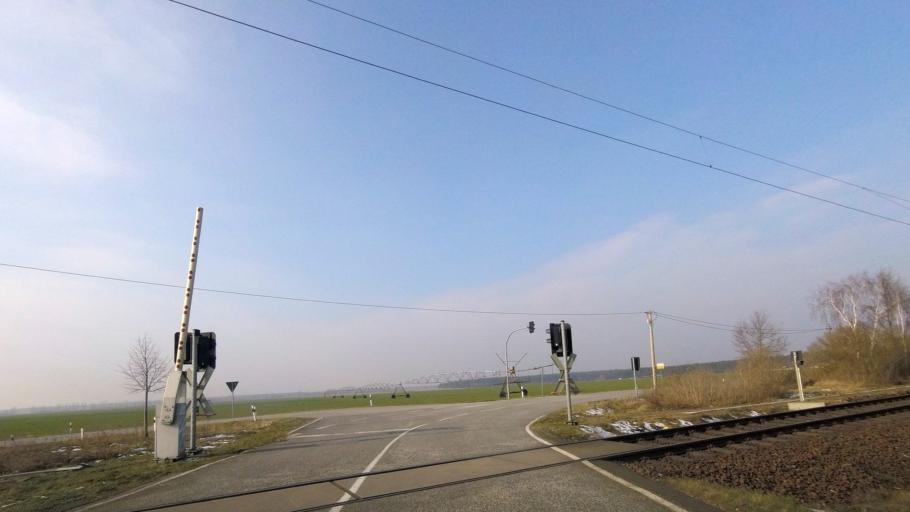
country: DE
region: Brandenburg
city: Juterbog
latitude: 51.8973
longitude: 13.0656
